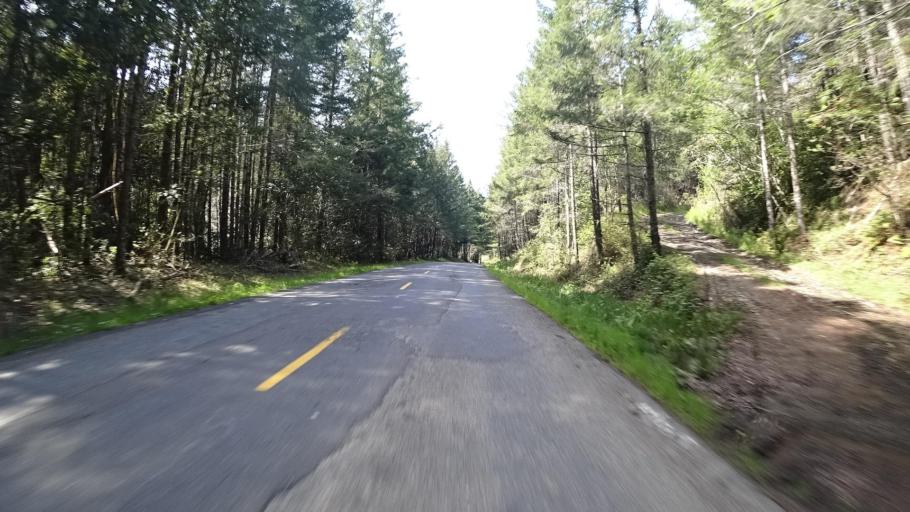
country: US
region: California
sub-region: Humboldt County
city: Redway
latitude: 40.4402
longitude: -123.7857
